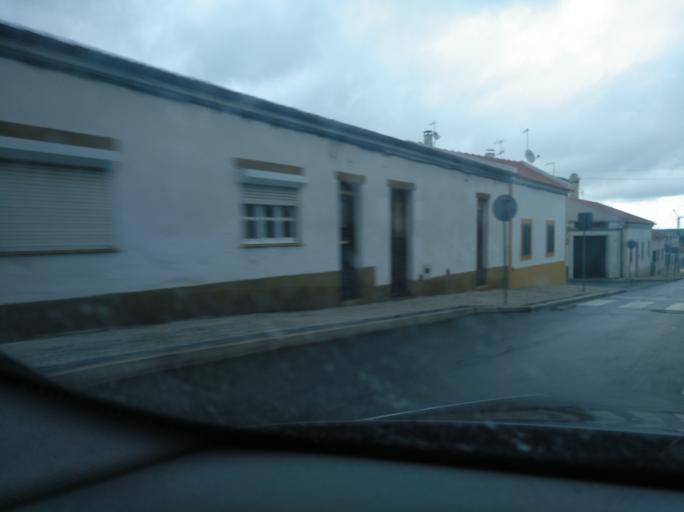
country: PT
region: Beja
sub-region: Aljustrel
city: Aljustrel
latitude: 37.8798
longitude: -8.1620
